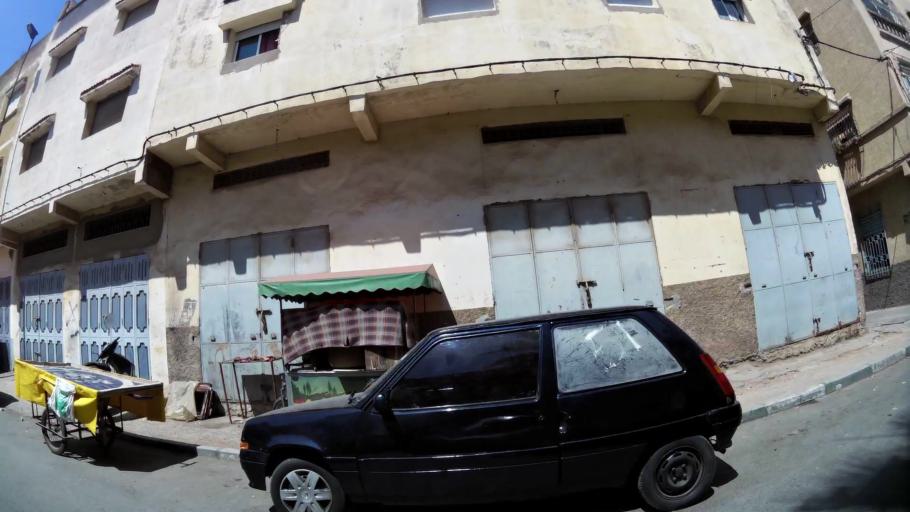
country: MA
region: Rabat-Sale-Zemmour-Zaer
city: Sale
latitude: 34.0663
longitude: -6.7775
